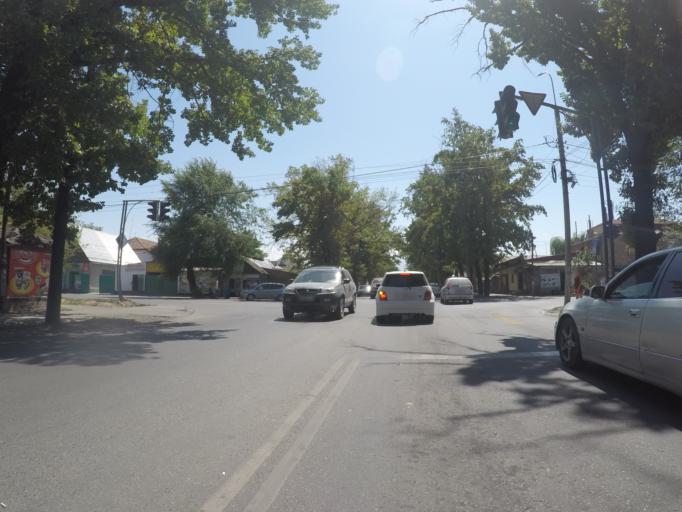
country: KG
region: Chuy
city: Bishkek
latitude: 42.8520
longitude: 74.5770
